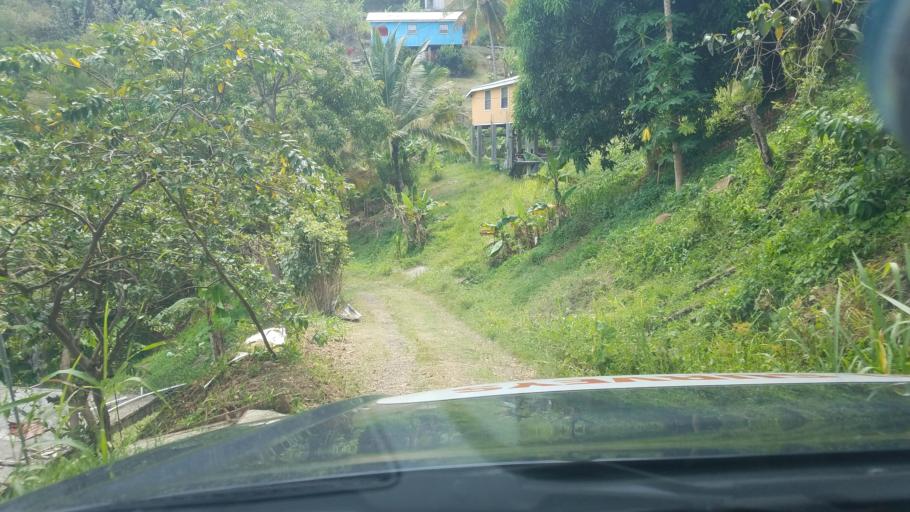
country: LC
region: Castries Quarter
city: Bisee
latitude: 14.0318
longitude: -60.9570
